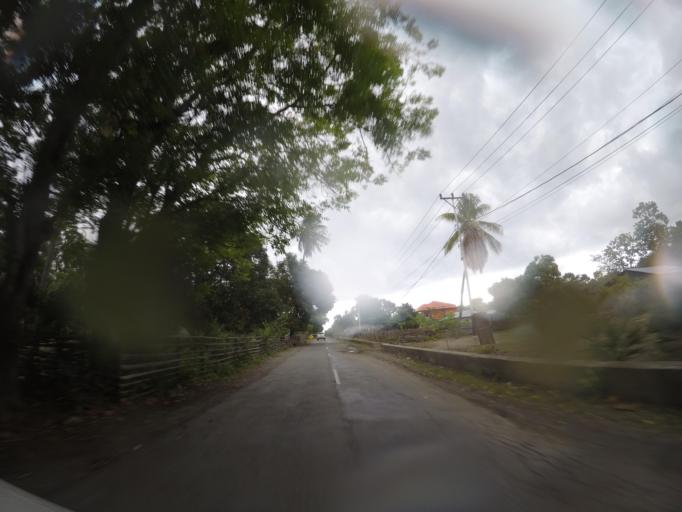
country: ID
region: East Nusa Tenggara
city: Atambua
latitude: -8.9557
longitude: 124.9800
